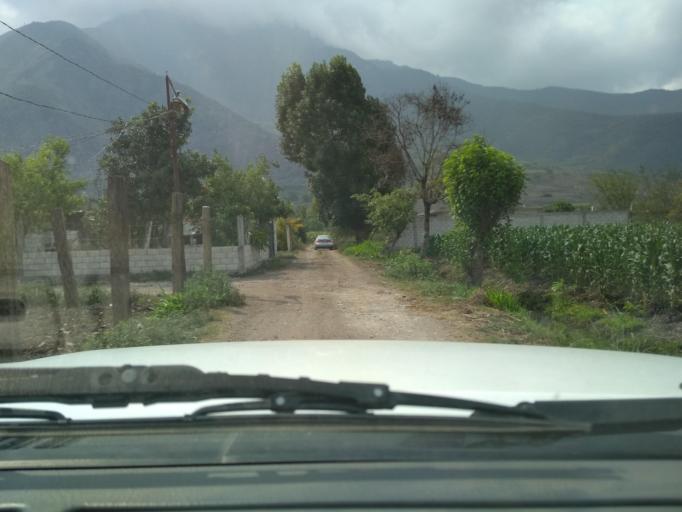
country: MX
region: Veracruz
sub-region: Acultzingo
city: Sierra de Agua
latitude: 18.7563
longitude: -97.2348
